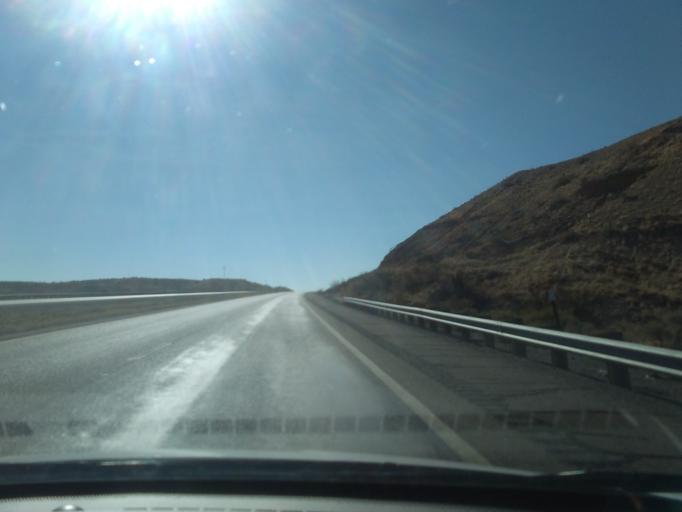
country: US
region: New Mexico
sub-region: Socorro County
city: Socorro
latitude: 34.3324
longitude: -106.8795
